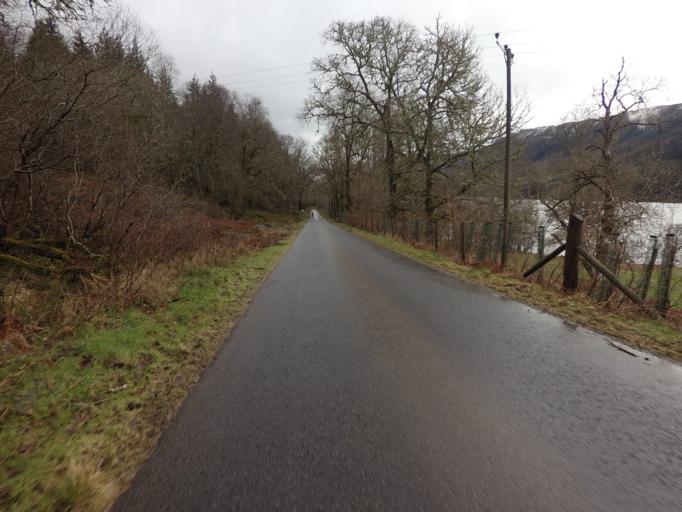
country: GB
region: Scotland
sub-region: West Dunbartonshire
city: Balloch
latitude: 56.2258
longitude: -4.5537
